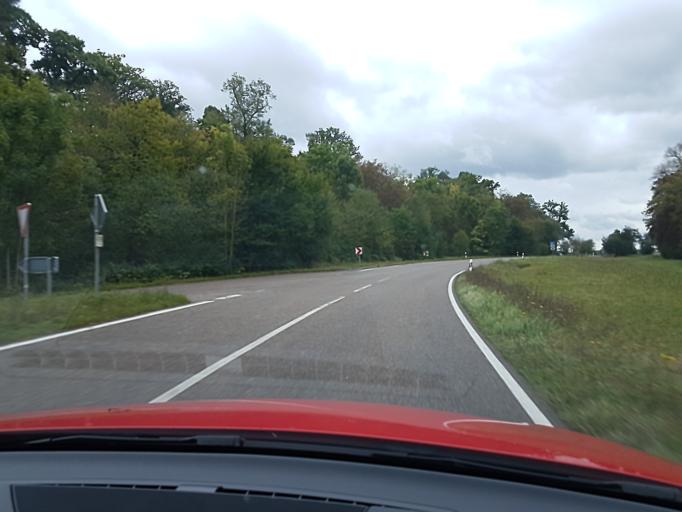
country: DE
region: Baden-Wuerttemberg
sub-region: Karlsruhe Region
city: Maulbronn
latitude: 48.9969
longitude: 8.8291
